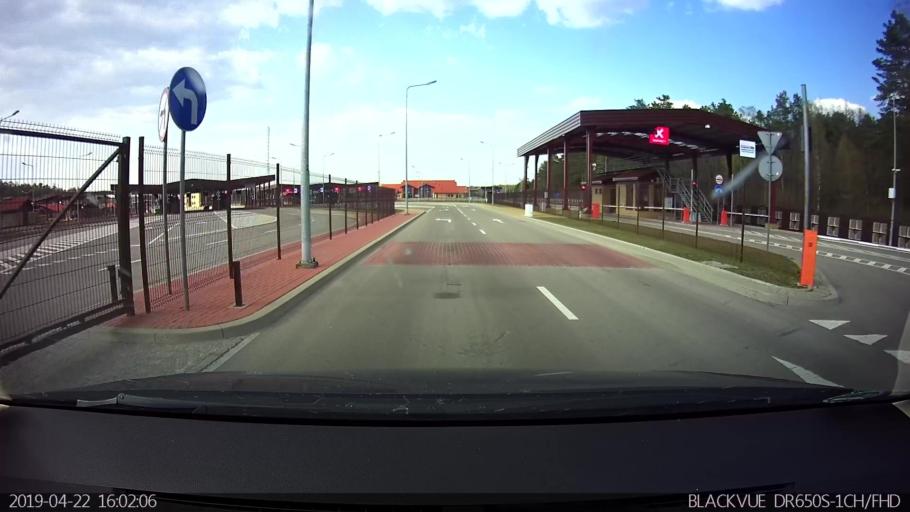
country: PL
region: Podlasie
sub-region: Powiat hajnowski
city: Czeremcha
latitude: 52.4736
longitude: 23.3576
